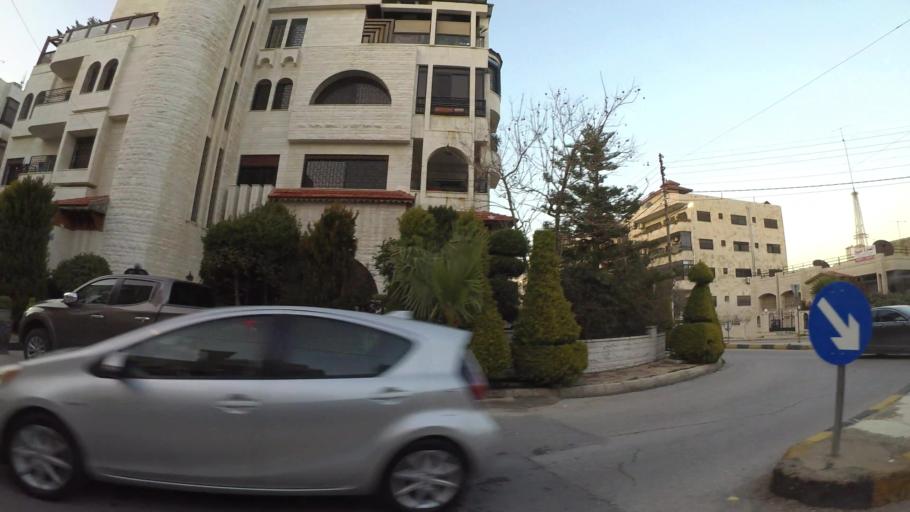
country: JO
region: Amman
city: Al Jubayhah
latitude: 31.9866
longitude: 35.8842
